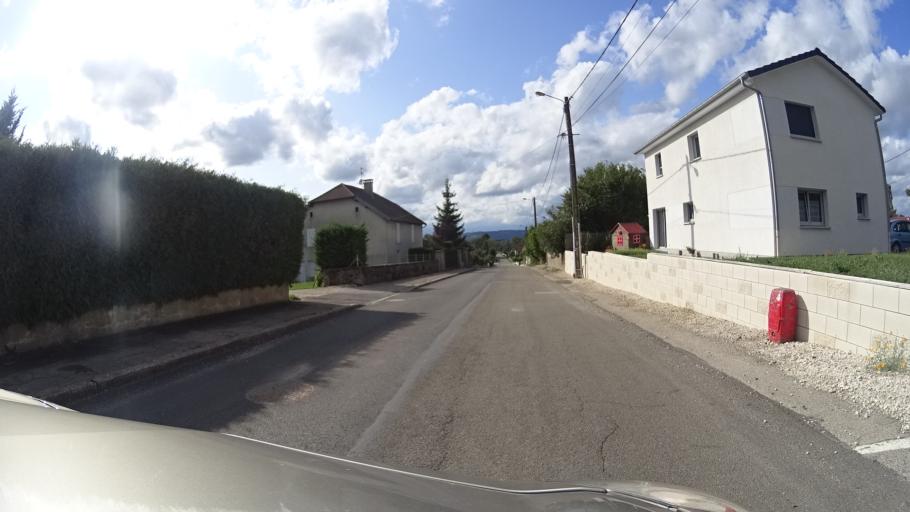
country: FR
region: Franche-Comte
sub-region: Departement du Doubs
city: Mamirolle
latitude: 47.2003
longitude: 6.1596
